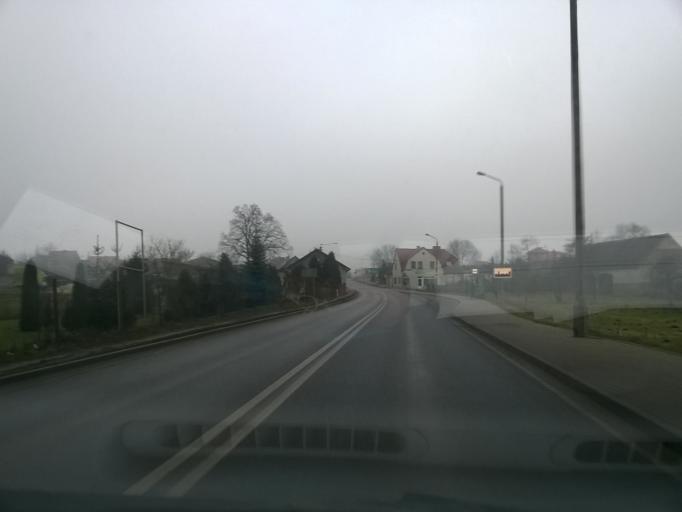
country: PL
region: Kujawsko-Pomorskie
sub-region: Powiat nakielski
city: Naklo nad Notecia
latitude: 53.1202
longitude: 17.6031
